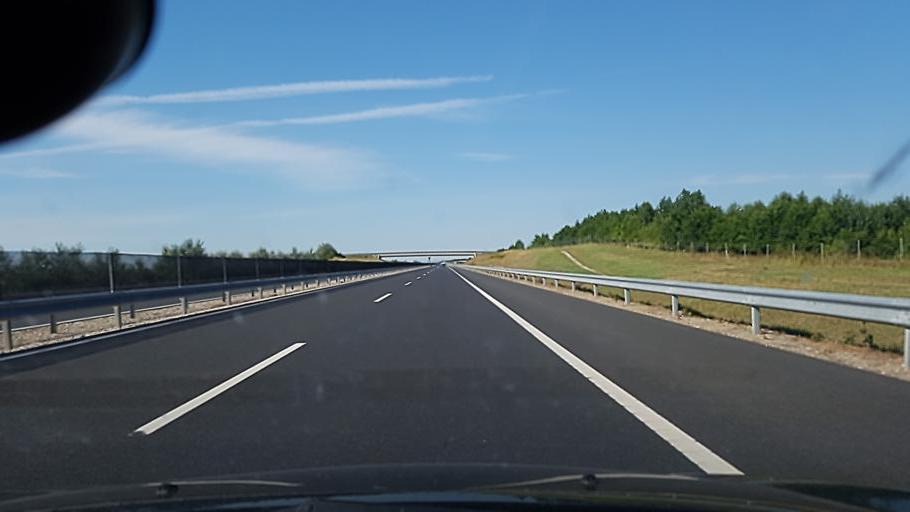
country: HU
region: Tolna
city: Dunaszentgyorgy
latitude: 46.5757
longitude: 18.8073
